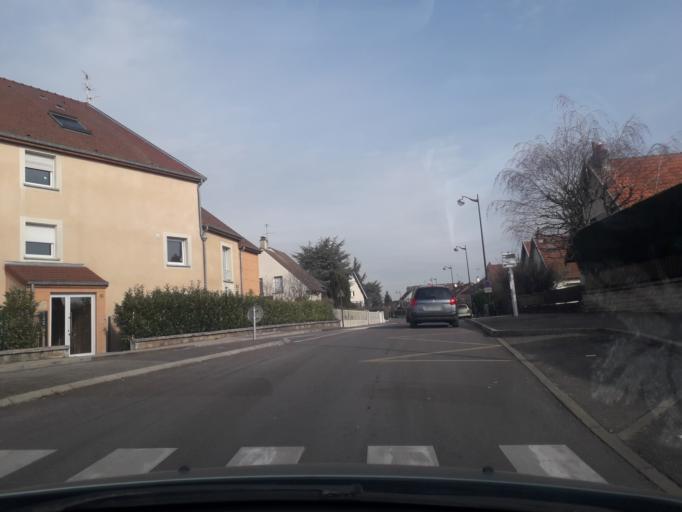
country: FR
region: Bourgogne
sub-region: Departement de la Cote-d'Or
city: Fontaine-les-Dijon
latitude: 47.3430
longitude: 5.0230
